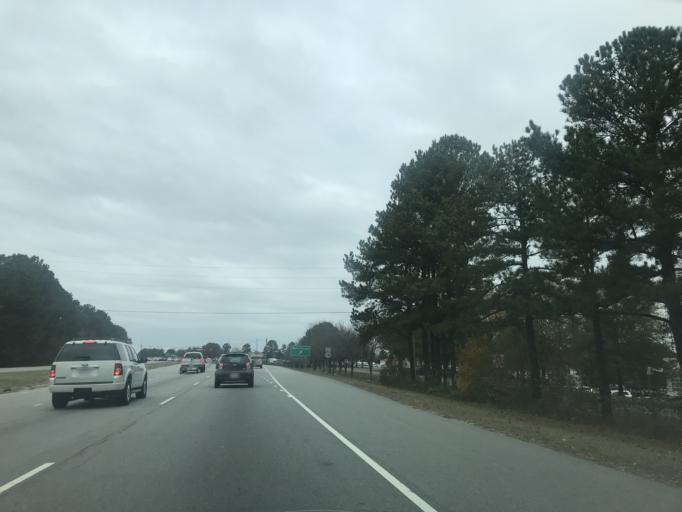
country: US
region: North Carolina
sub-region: Wake County
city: Wake Forest
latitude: 35.9434
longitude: -78.5395
